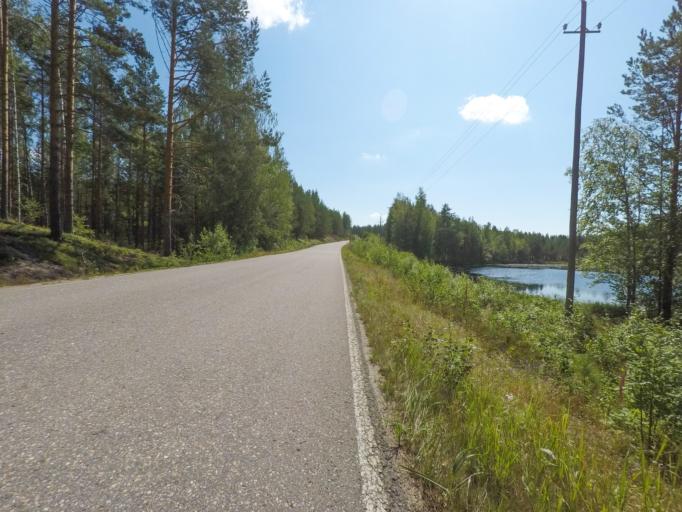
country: FI
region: Southern Savonia
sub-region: Mikkeli
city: Puumala
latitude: 61.4628
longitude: 28.1733
